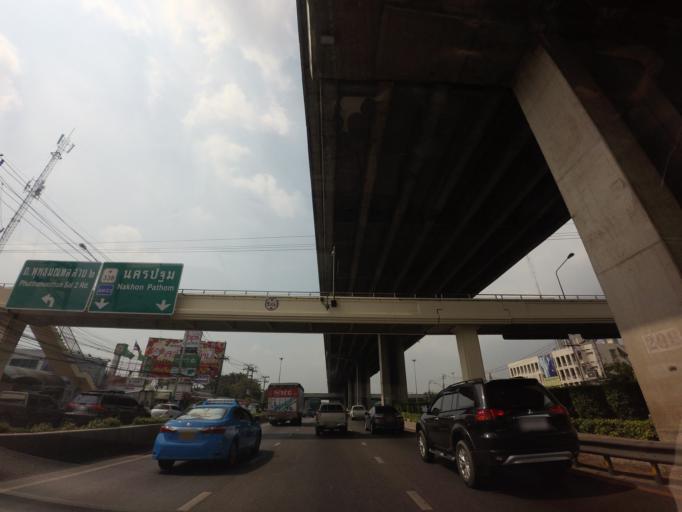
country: TH
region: Bangkok
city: Taling Chan
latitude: 13.7843
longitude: 100.3962
